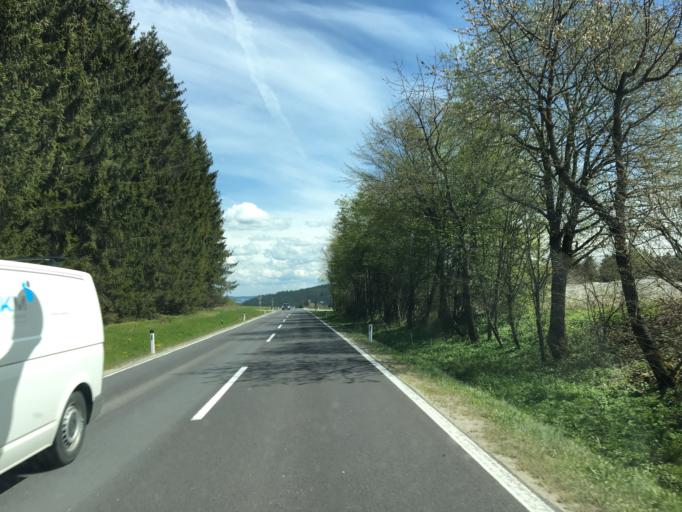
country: AT
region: Upper Austria
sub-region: Politischer Bezirk Urfahr-Umgebung
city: Schenkenfelden
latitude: 48.5181
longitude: 14.3377
